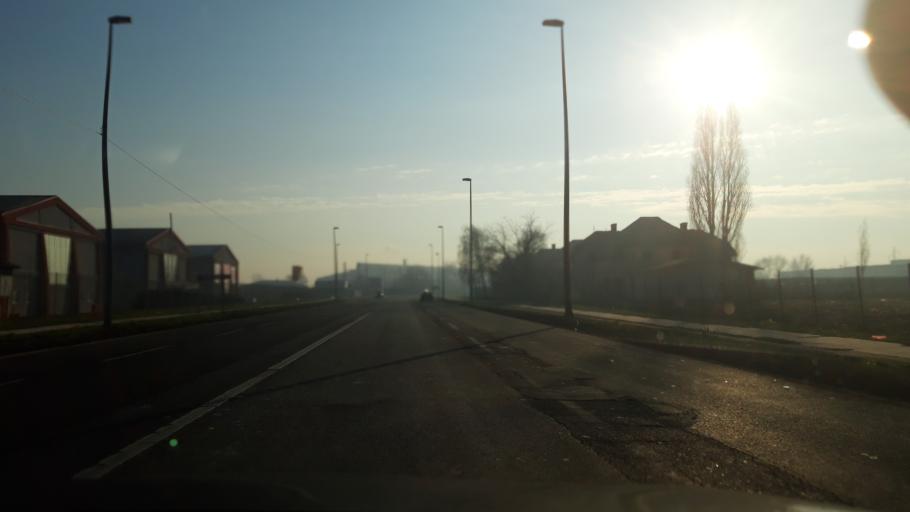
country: RS
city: Pocerski Pricinovic
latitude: 44.7470
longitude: 19.7170
